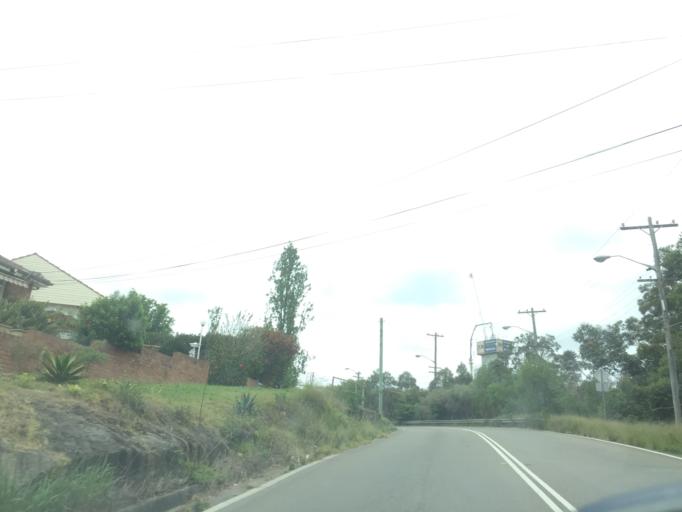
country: AU
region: New South Wales
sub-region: Lane Cove
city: Lane Cove West
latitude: -33.8022
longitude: 151.1485
